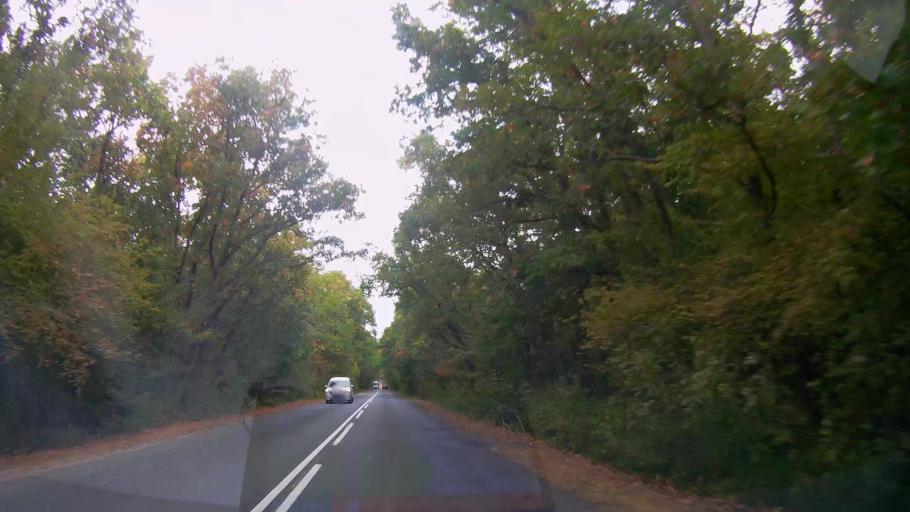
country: BG
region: Burgas
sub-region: Obshtina Primorsko
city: Primorsko
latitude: 42.2958
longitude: 27.7298
